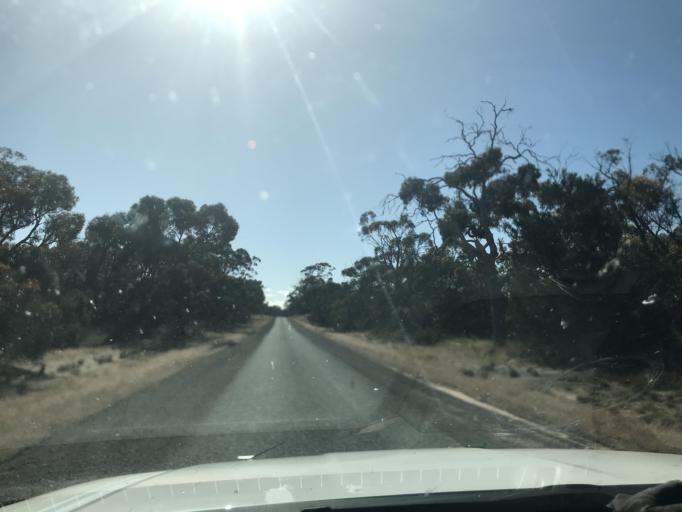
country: AU
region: Victoria
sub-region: Horsham
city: Horsham
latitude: -37.0235
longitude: 141.6883
